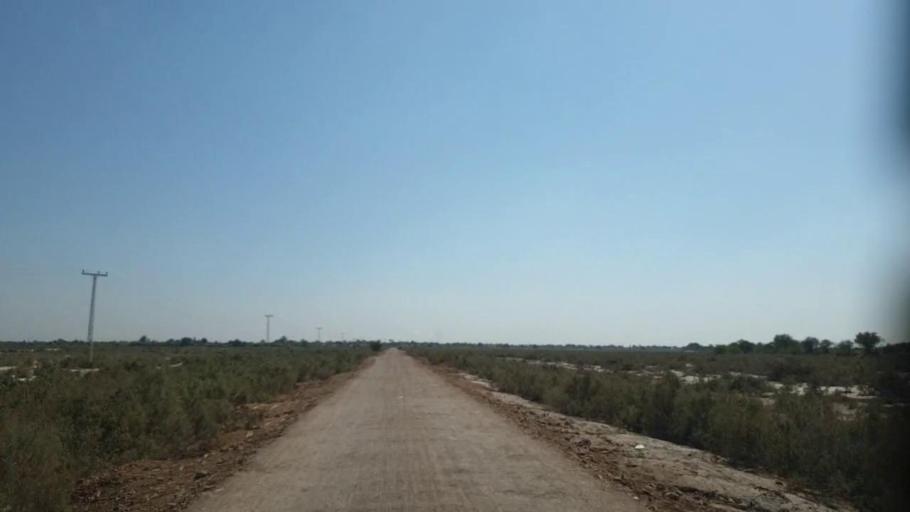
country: PK
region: Sindh
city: Mirpur Khas
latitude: 25.5881
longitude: 69.1070
